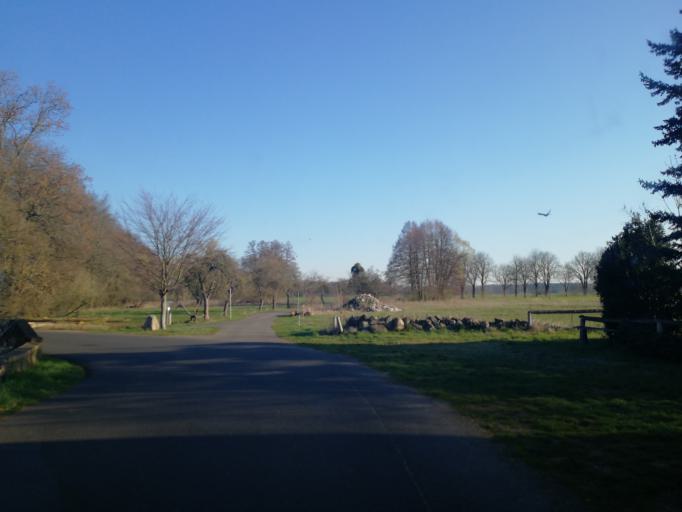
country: DE
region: Brandenburg
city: Drahnsdorf
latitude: 51.9263
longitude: 13.5995
